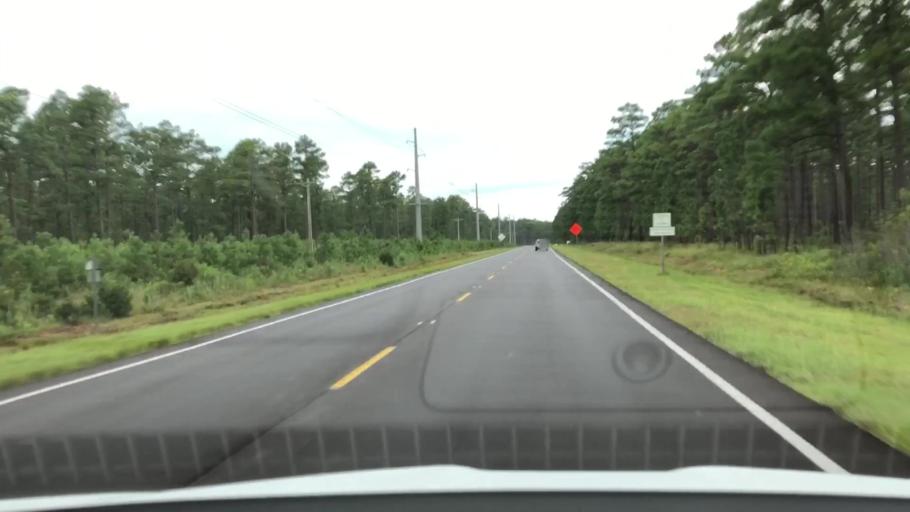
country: US
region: North Carolina
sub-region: Onslow County
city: Swansboro
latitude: 34.8129
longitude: -77.1397
